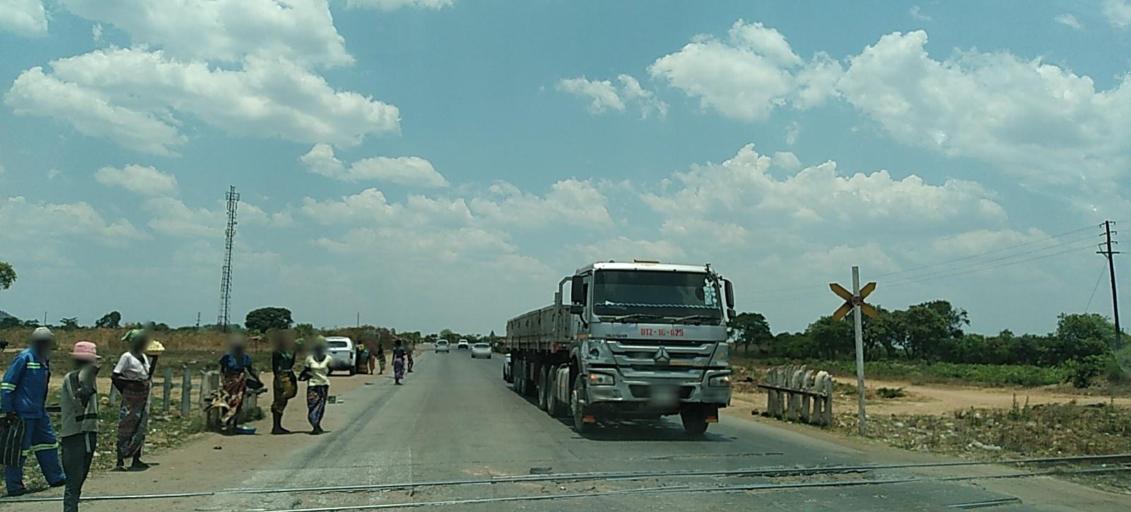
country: ZM
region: Central
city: Kapiri Mposhi
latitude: -13.8928
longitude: 28.6579
